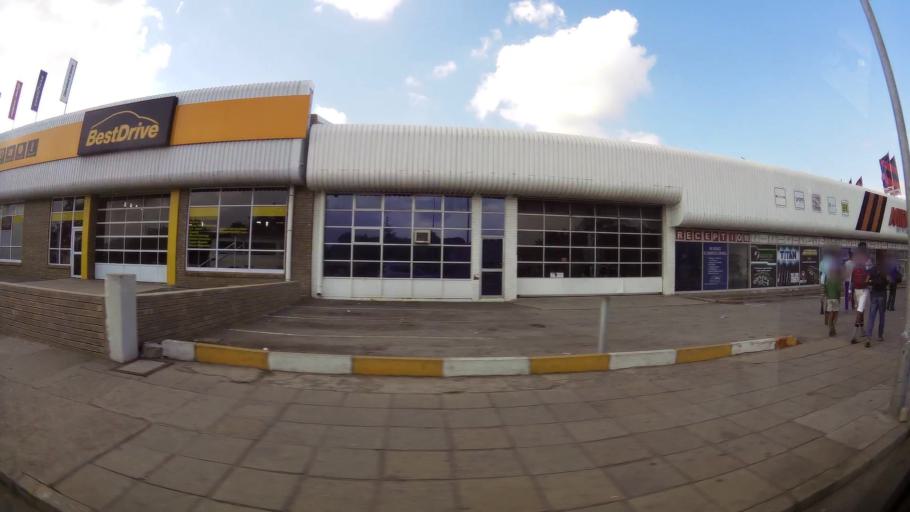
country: ZA
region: Eastern Cape
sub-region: Nelson Mandela Bay Metropolitan Municipality
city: Uitenhage
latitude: -33.7692
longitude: 25.3954
